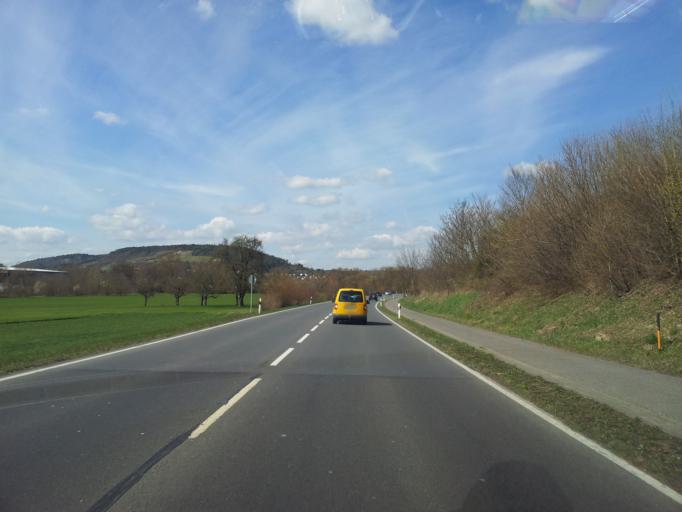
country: DE
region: Baden-Wuerttemberg
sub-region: Regierungsbezirk Stuttgart
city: Lauda-Konigshofen
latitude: 49.5636
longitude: 9.7180
